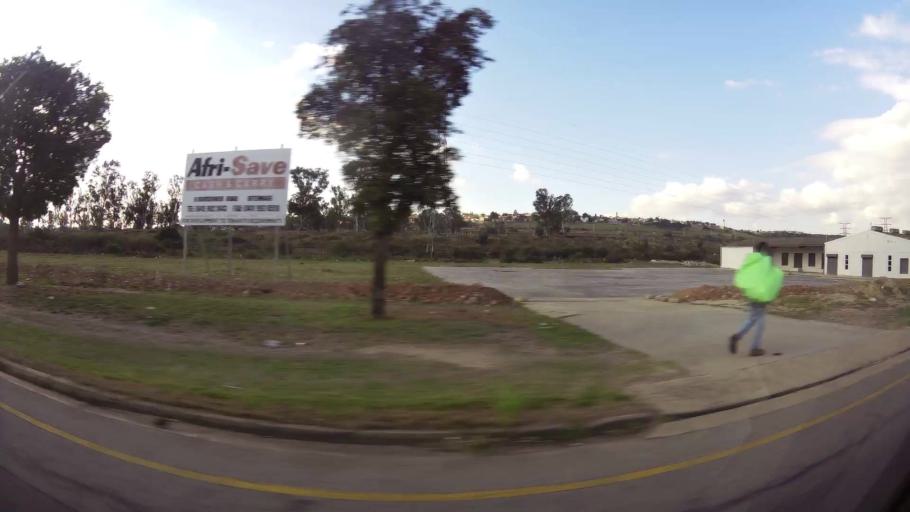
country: ZA
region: Eastern Cape
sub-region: Nelson Mandela Bay Metropolitan Municipality
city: Uitenhage
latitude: -33.7804
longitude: 25.4134
